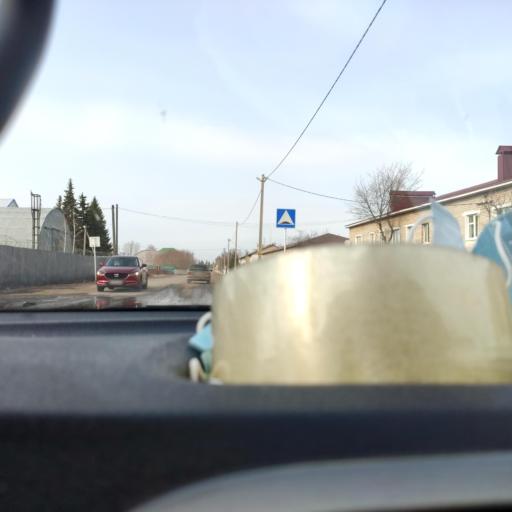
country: RU
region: Bashkortostan
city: Ulukulevo
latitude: 54.3734
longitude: 56.4495
